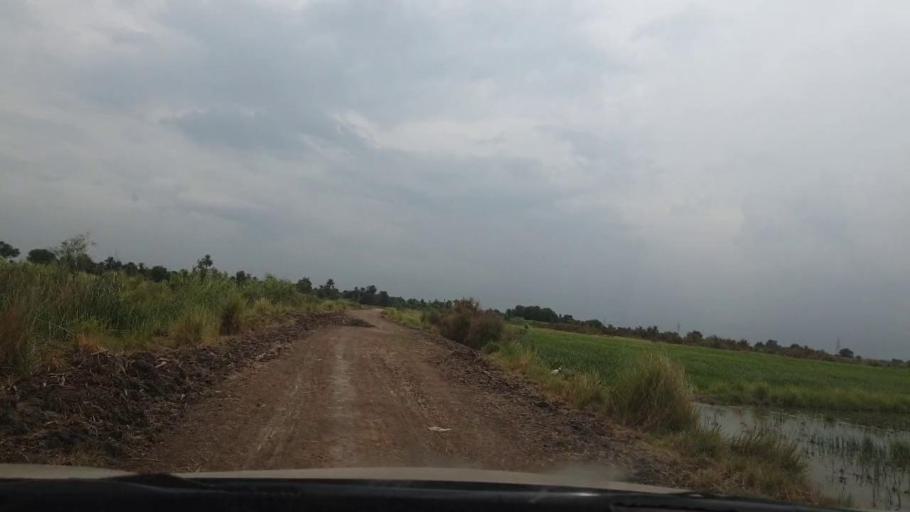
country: PK
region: Sindh
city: Ratodero
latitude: 27.7992
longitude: 68.3131
